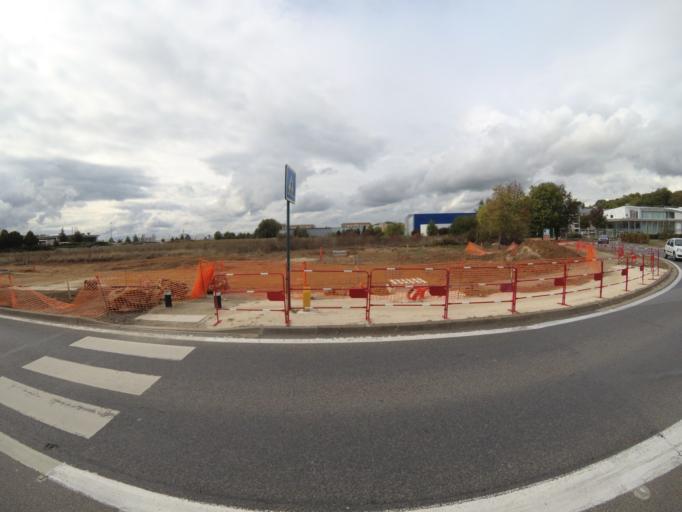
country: FR
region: Ile-de-France
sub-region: Departement de Seine-et-Marne
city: Montevrain
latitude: 48.8657
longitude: 2.7649
